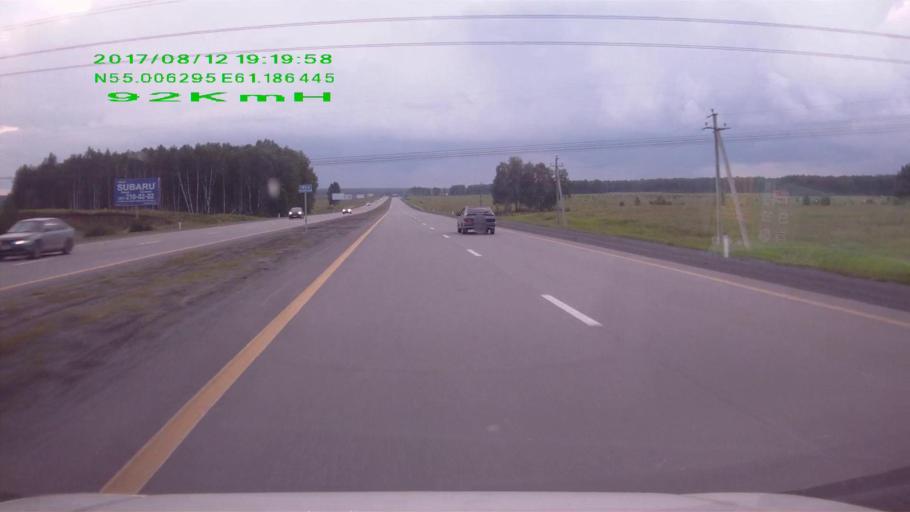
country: RU
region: Chelyabinsk
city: Sargazy
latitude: 55.0061
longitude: 61.1833
